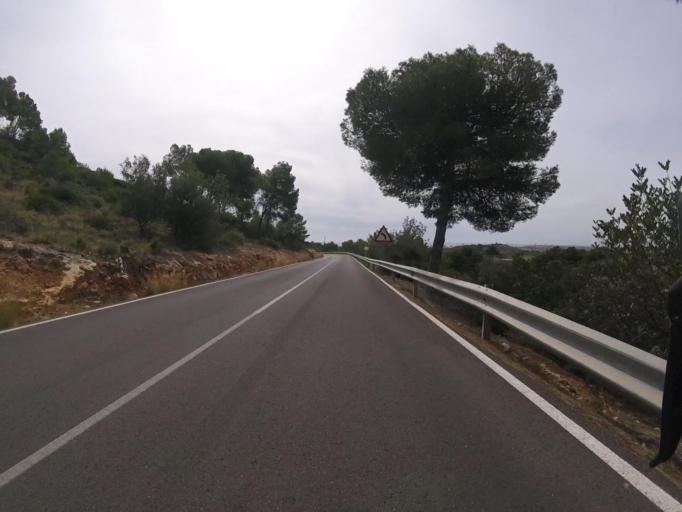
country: ES
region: Valencia
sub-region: Provincia de Castello
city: Benicassim
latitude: 40.0563
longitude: 0.0454
